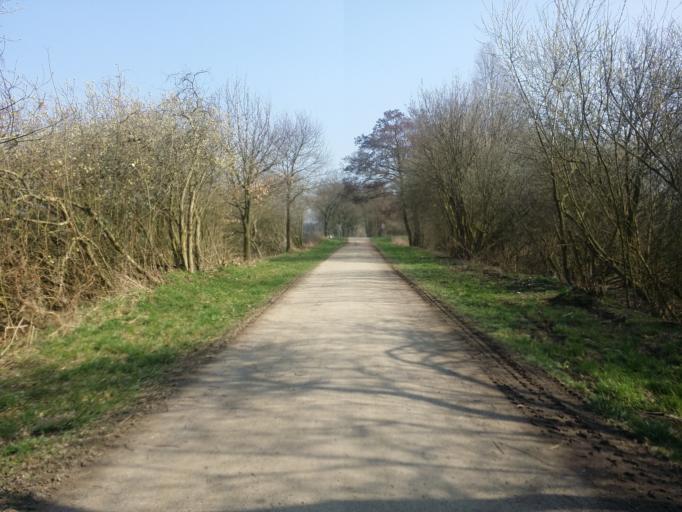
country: DE
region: Lower Saxony
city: Delmenhorst
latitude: 53.0150
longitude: 8.6630
